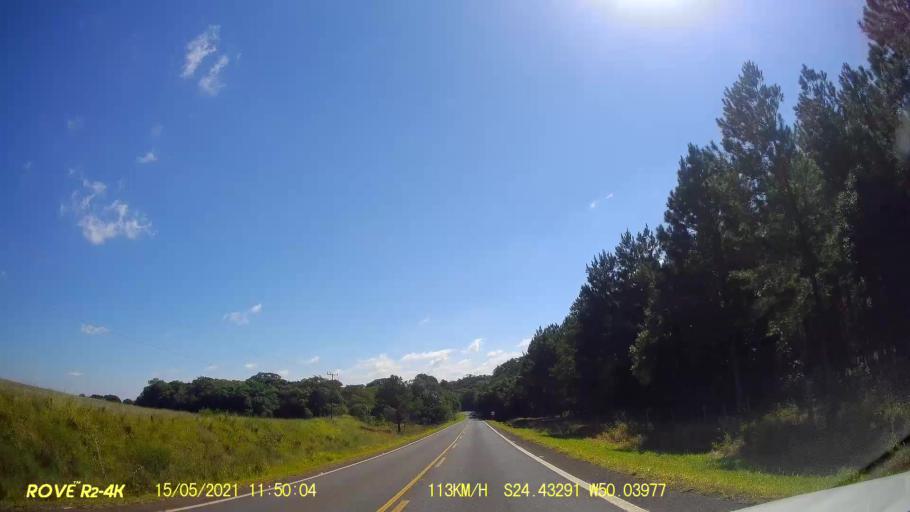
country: BR
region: Parana
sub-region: Pirai Do Sul
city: Pirai do Sul
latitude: -24.4329
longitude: -50.0397
